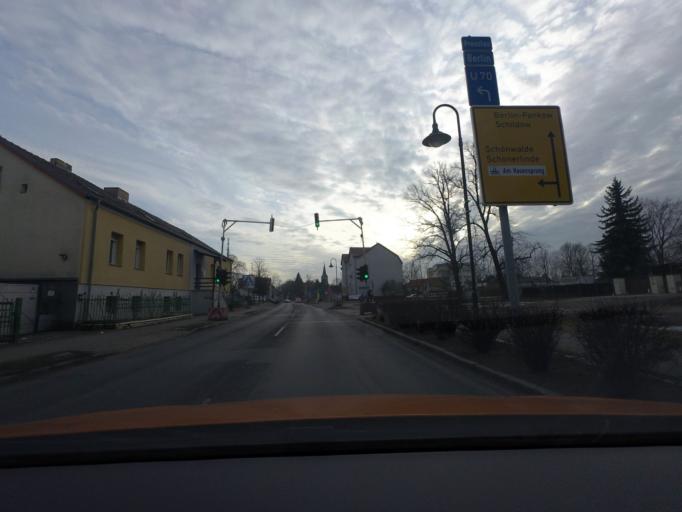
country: DE
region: Berlin
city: Blankenfelde
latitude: 52.6665
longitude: 13.3791
